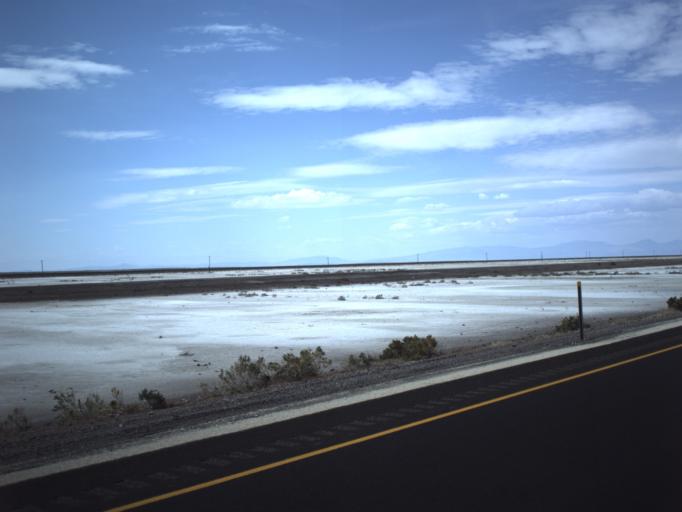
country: US
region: Utah
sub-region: Tooele County
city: Wendover
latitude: 40.7319
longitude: -113.5034
